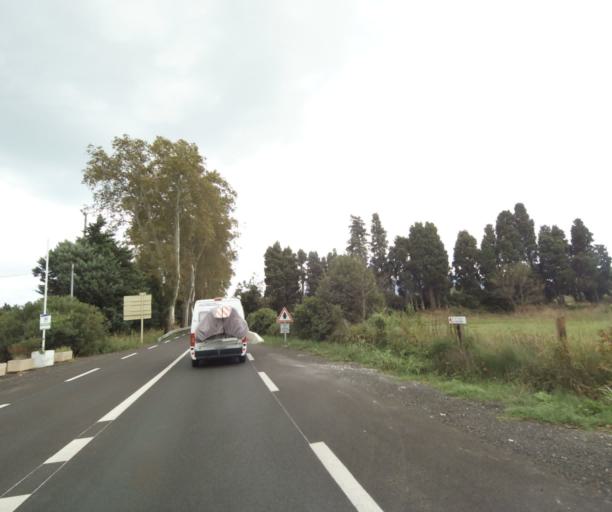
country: FR
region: Languedoc-Roussillon
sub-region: Departement des Pyrenees-Orientales
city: Elne
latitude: 42.5916
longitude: 2.9793
